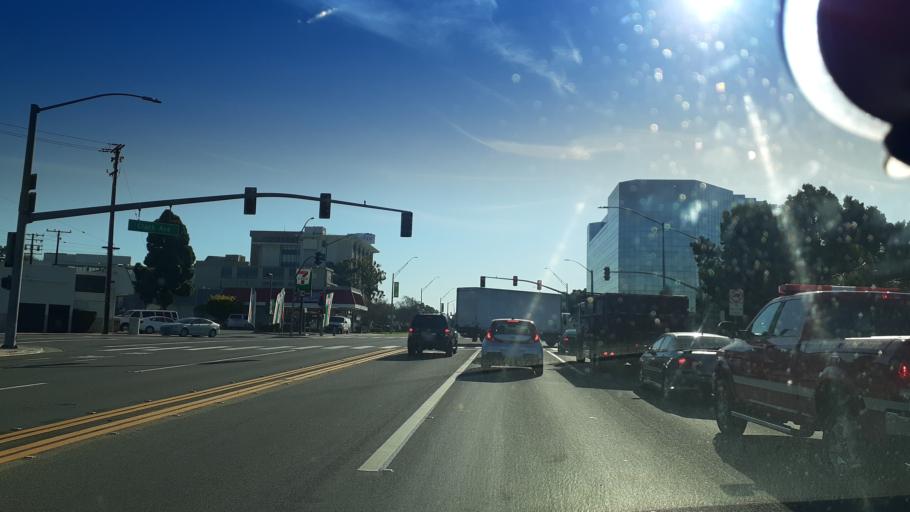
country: US
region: California
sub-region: Los Angeles County
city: Signal Hill
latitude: 33.7842
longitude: -118.1346
